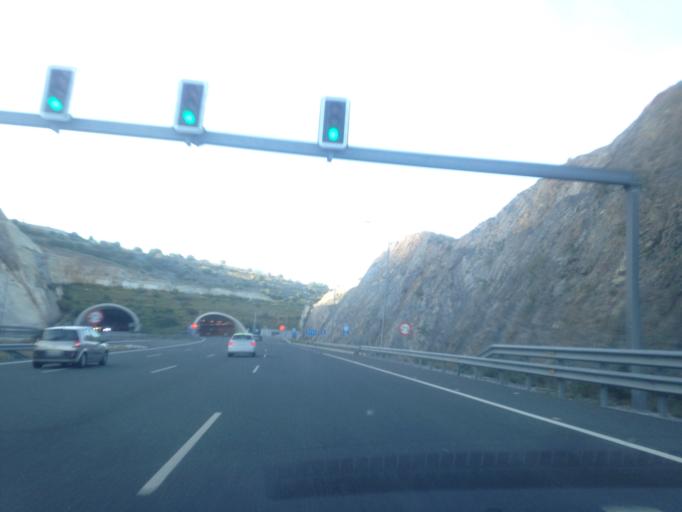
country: ES
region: Andalusia
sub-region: Provincia de Malaga
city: Torremolinos
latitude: 36.6467
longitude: -4.5125
